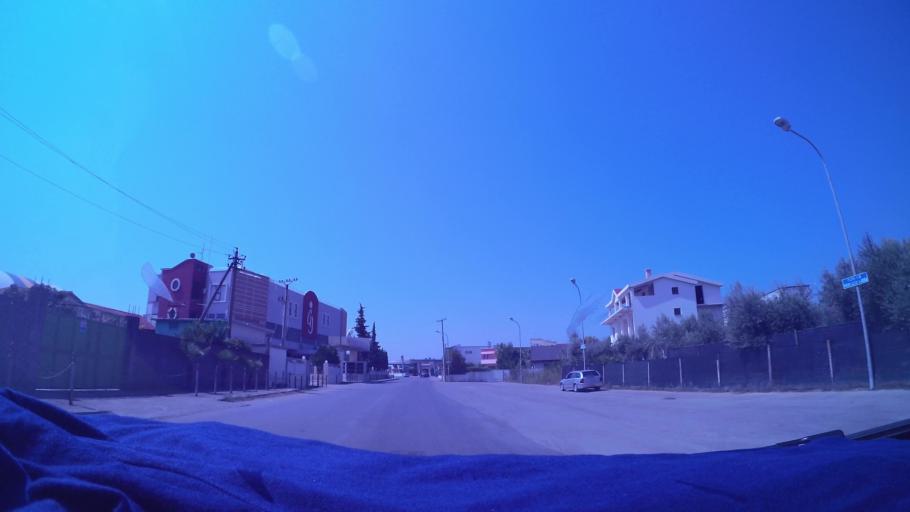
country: AL
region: Durres
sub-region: Rrethi i Durresit
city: Xhafzotaj
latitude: 41.3557
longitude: 19.5459
